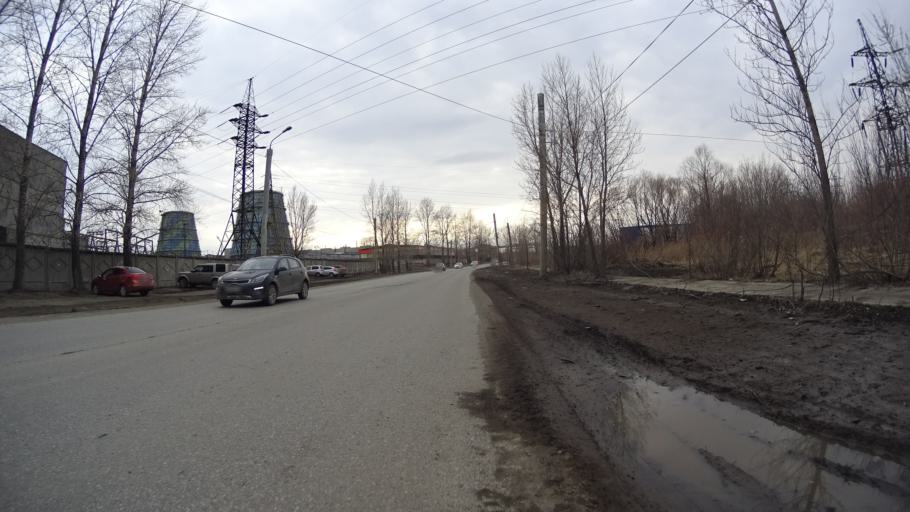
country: RU
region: Chelyabinsk
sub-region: Gorod Chelyabinsk
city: Chelyabinsk
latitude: 55.1564
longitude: 61.4973
